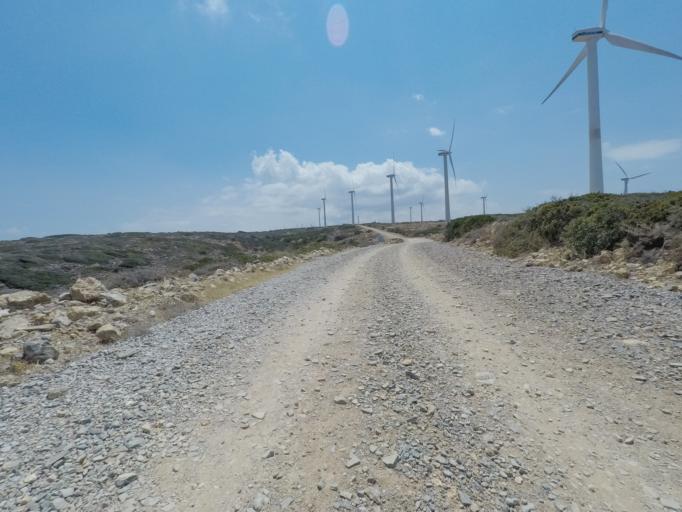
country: GR
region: Crete
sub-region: Nomos Lasithiou
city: Elounda
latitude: 35.3294
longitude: 25.7589
